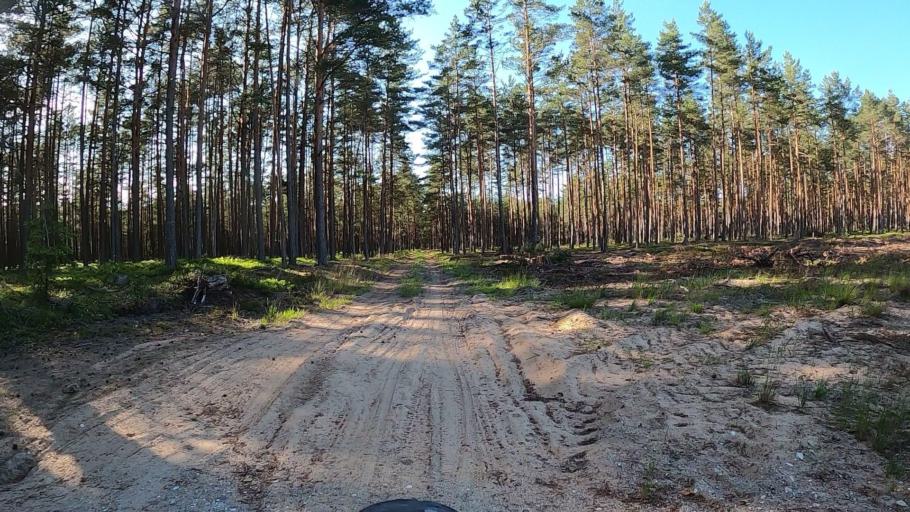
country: LV
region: Carnikava
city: Carnikava
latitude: 57.1059
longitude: 24.2474
